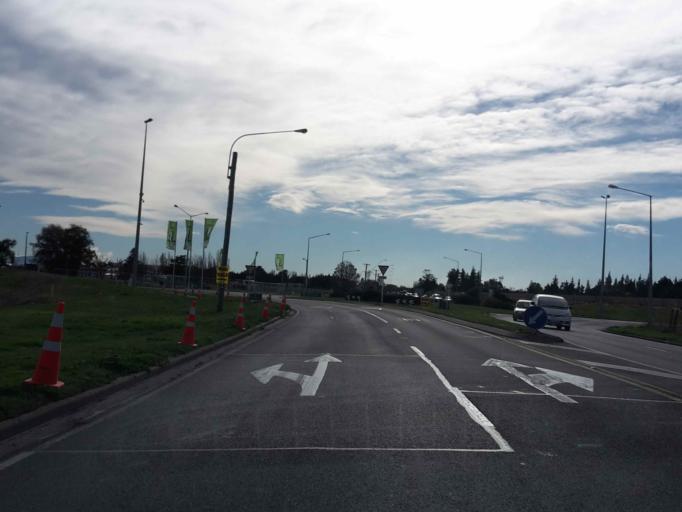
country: NZ
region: Canterbury
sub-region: Christchurch City
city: Christchurch
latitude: -43.4939
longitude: 172.5494
